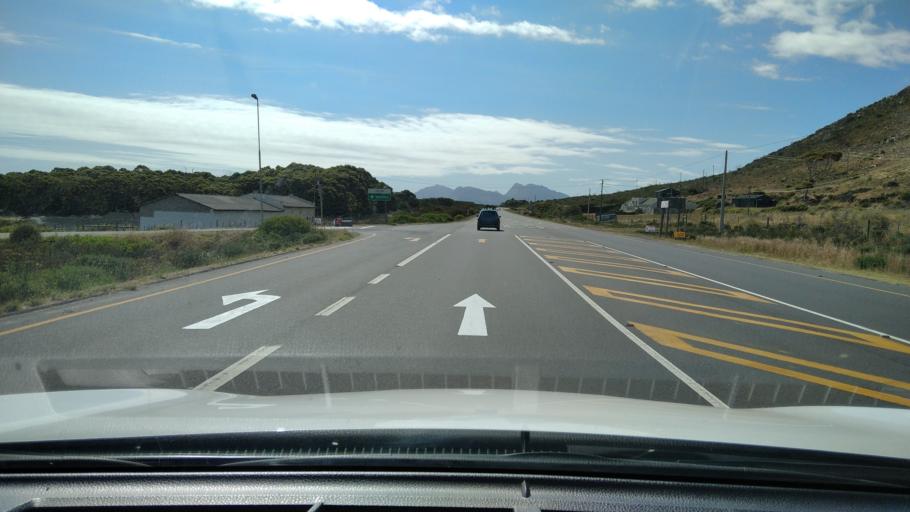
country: ZA
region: Western Cape
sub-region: Overberg District Municipality
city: Hermanus
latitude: -34.4059
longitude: 19.1496
